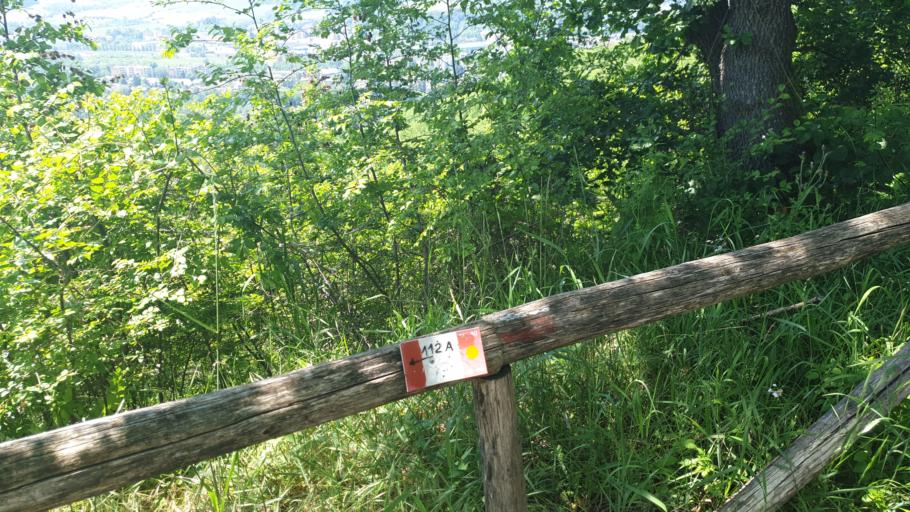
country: IT
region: Emilia-Romagna
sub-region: Provincia di Bologna
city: Casalecchio di Reno
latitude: 44.4755
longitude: 11.2917
